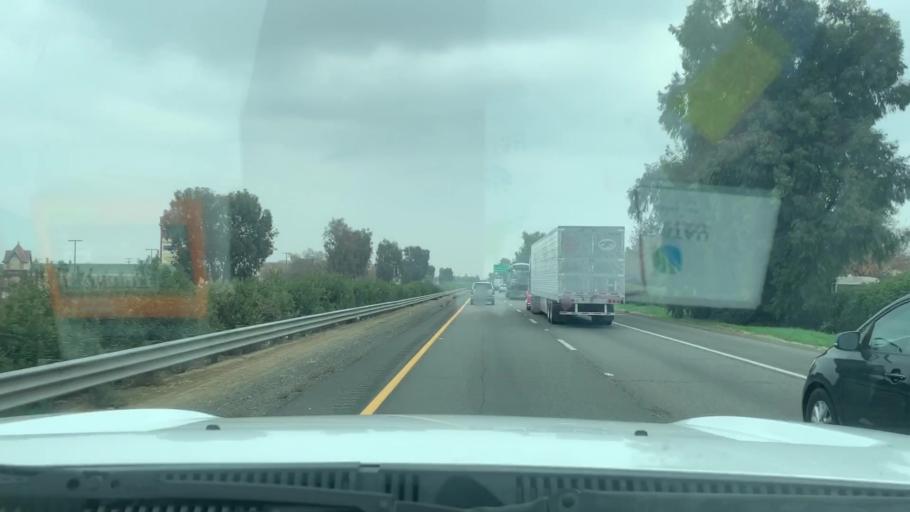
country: US
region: California
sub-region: Tulare County
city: Tulare
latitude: 36.2306
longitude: -119.3387
